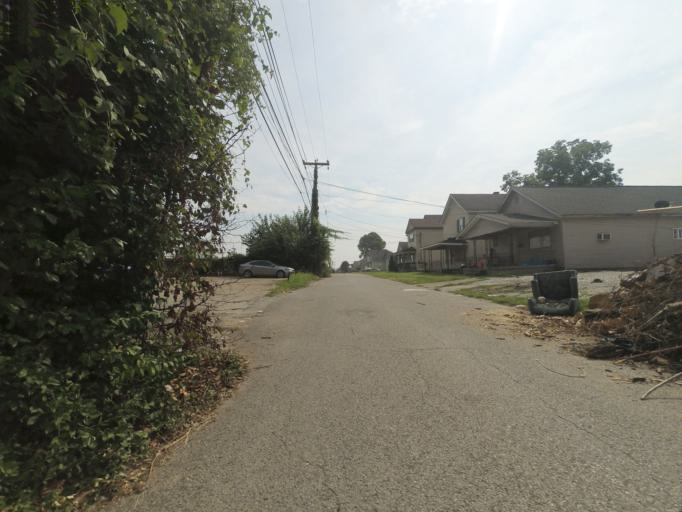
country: US
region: West Virginia
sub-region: Cabell County
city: Huntington
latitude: 38.4203
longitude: -82.4263
